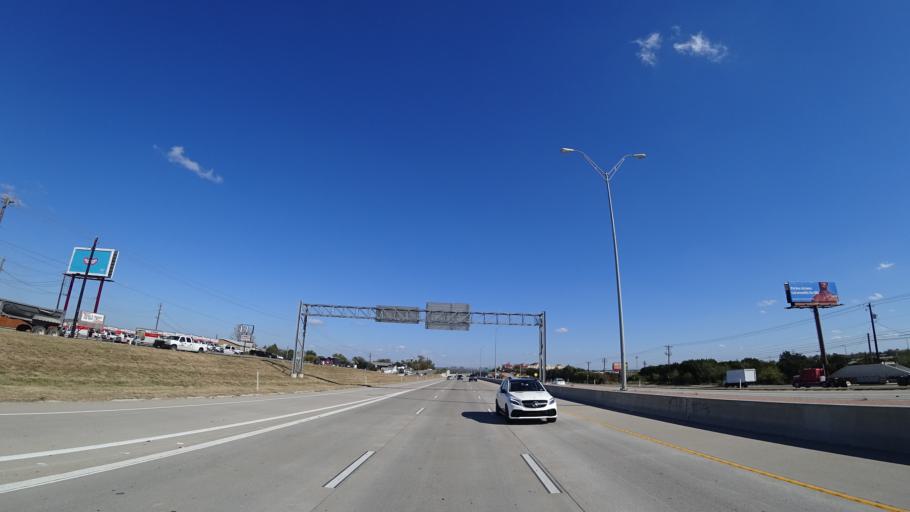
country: US
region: Texas
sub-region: Travis County
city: Austin
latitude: 30.2158
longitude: -97.6990
